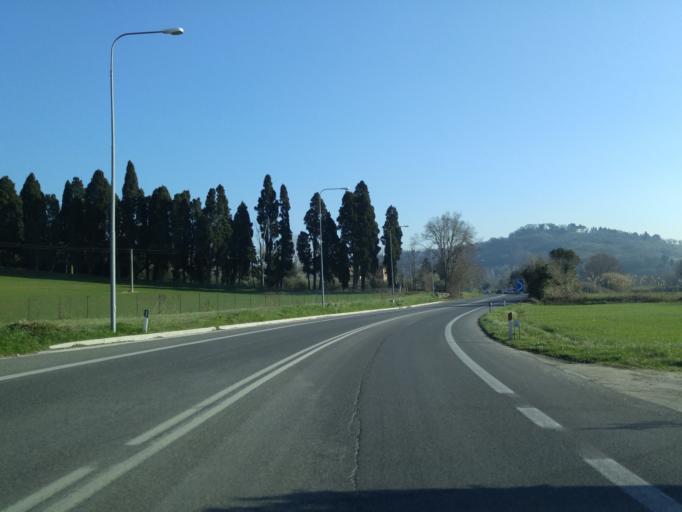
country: IT
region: The Marches
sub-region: Provincia di Pesaro e Urbino
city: Gradara
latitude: 43.9521
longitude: 12.7846
